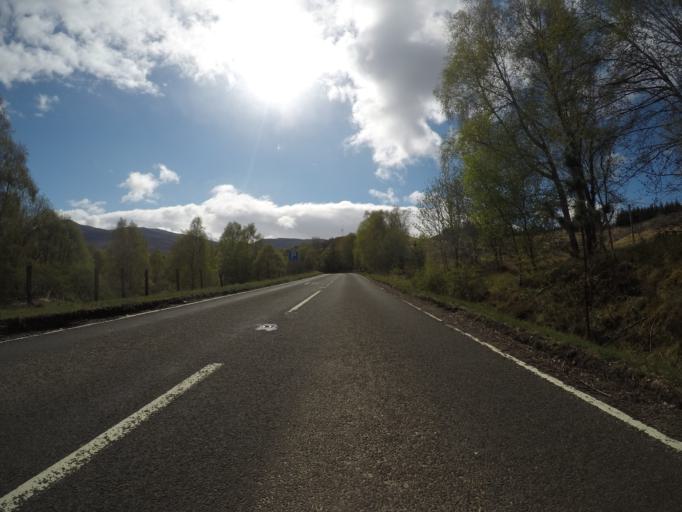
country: GB
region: Scotland
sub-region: Highland
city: Spean Bridge
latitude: 57.1435
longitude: -4.9577
